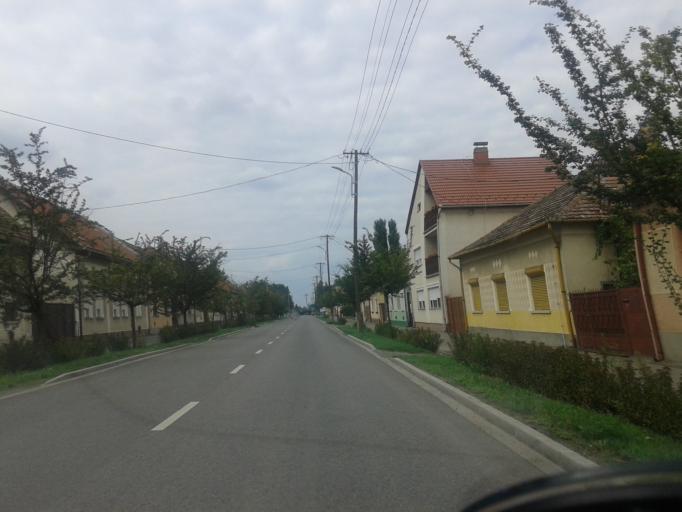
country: HU
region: Csongrad
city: Morahalom
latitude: 46.2134
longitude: 19.8908
